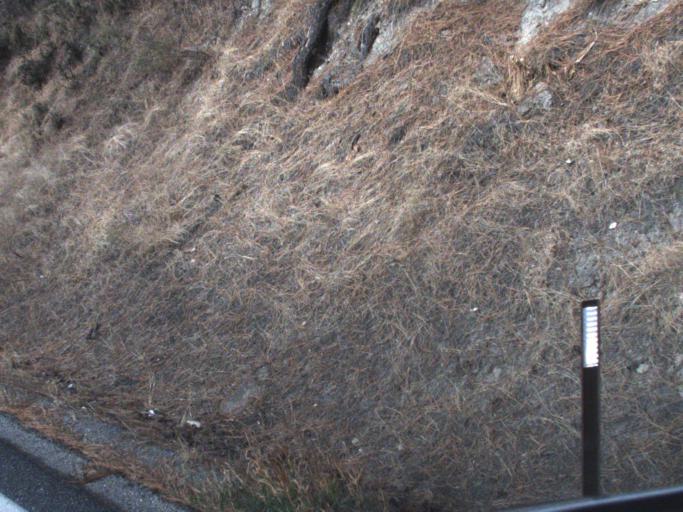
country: US
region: Washington
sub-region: Stevens County
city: Kettle Falls
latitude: 48.7257
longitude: -118.0422
